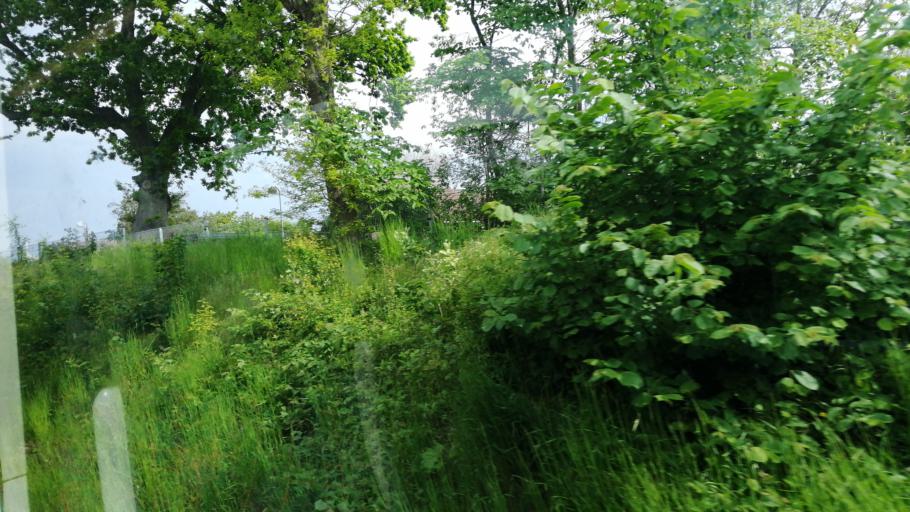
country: DK
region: Capital Region
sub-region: Gribskov Kommune
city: Gilleleje
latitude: 56.1205
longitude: 12.3113
